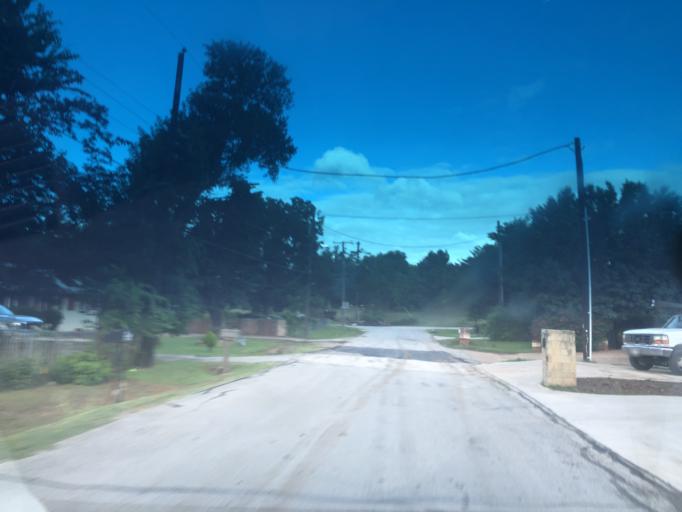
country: US
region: Texas
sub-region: Dallas County
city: Irving
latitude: 32.8064
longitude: -97.0043
